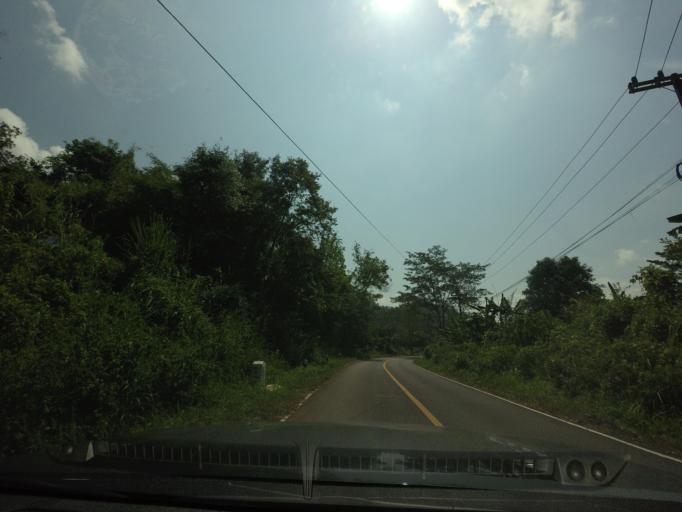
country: TH
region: Nan
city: Bo Kluea
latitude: 19.0412
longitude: 101.1708
